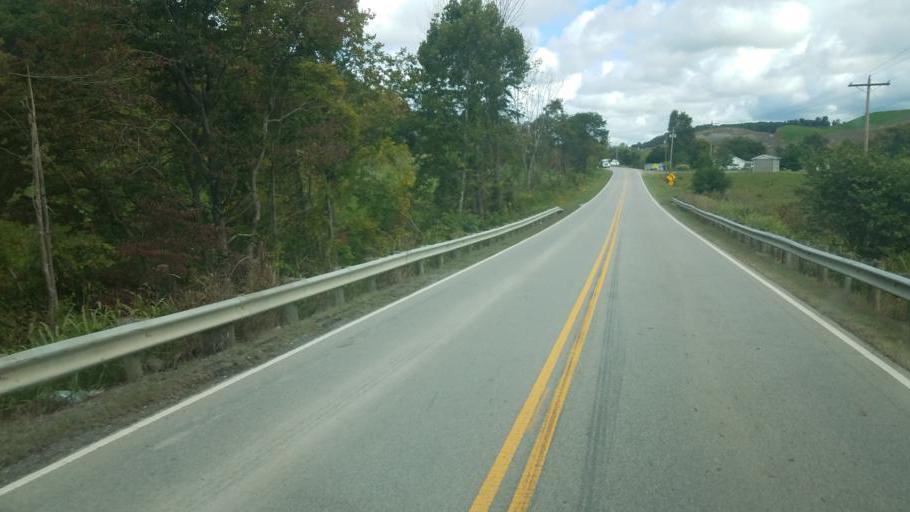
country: US
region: Ohio
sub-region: Scioto County
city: Lucasville
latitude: 38.8596
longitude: -82.9055
